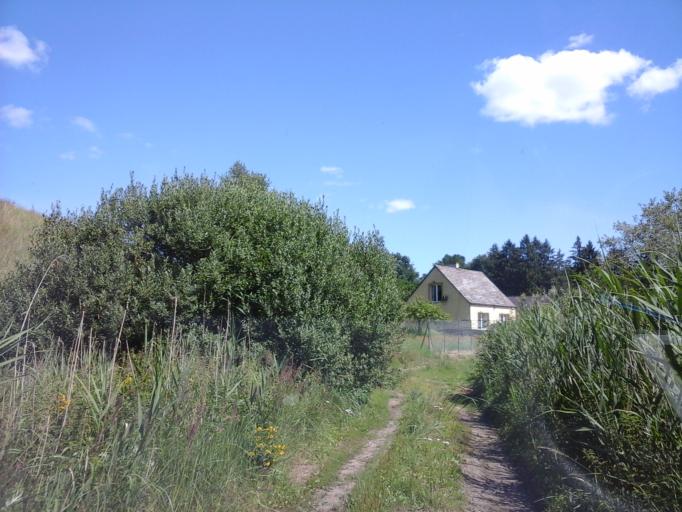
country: PL
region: West Pomeranian Voivodeship
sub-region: Powiat choszczenski
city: Drawno
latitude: 53.2877
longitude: 15.6804
